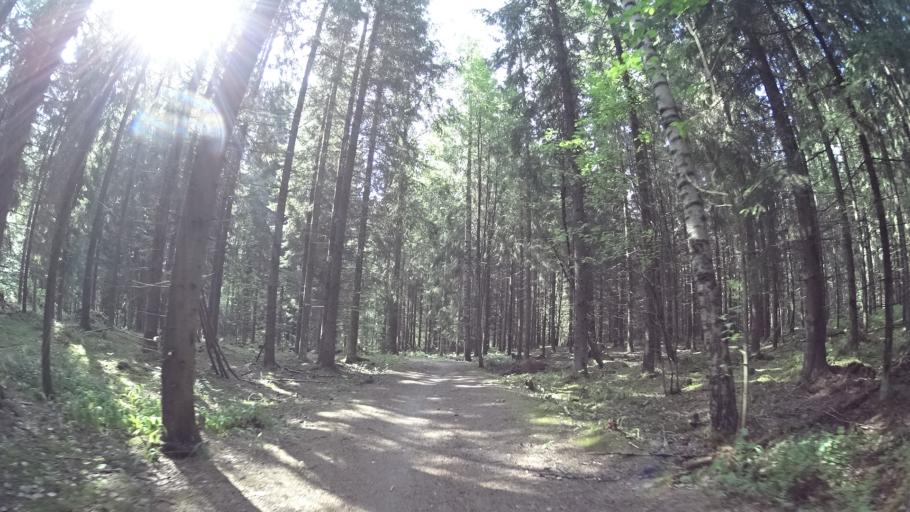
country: FI
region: Uusimaa
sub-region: Helsinki
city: Teekkarikylae
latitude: 60.2727
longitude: 24.9027
